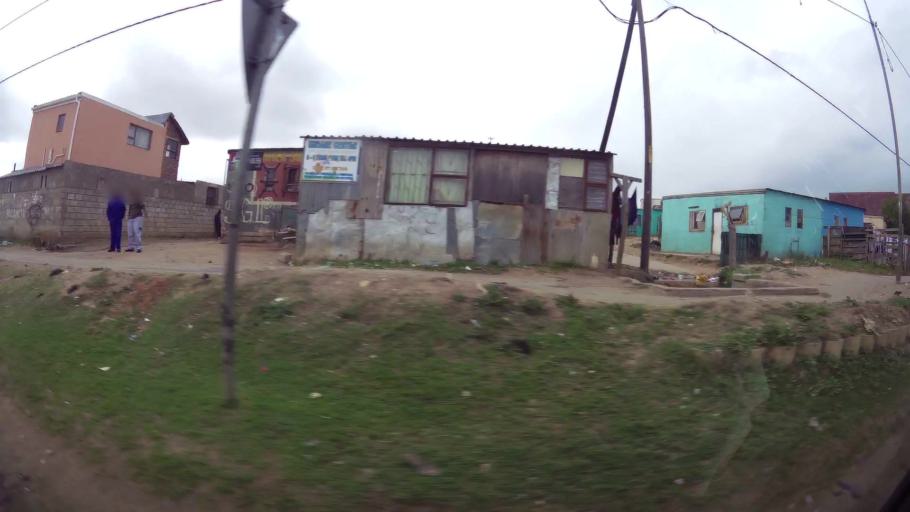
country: ZA
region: Eastern Cape
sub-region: Nelson Mandela Bay Metropolitan Municipality
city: Port Elizabeth
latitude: -33.8850
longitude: 25.5572
